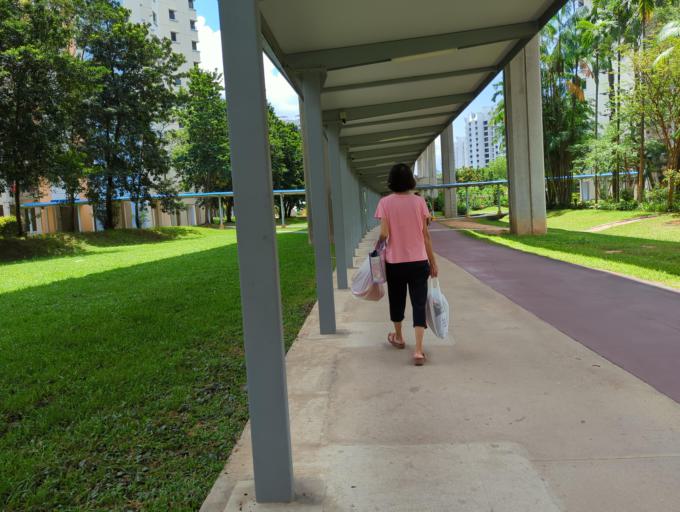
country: MY
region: Johor
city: Kampung Pasir Gudang Baru
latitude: 1.3934
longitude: 103.8961
